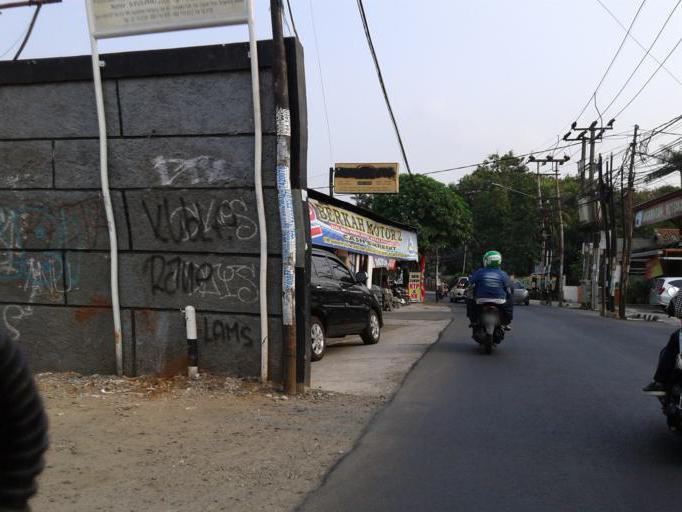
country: ID
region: Banten
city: South Tangerang
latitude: -6.2937
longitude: 106.7467
